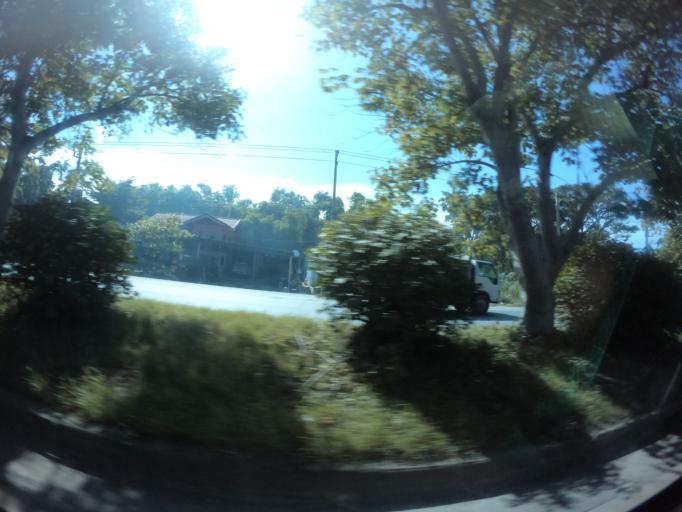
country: TH
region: Nakhon Nayok
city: Ban Na
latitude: 14.2095
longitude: 101.0689
